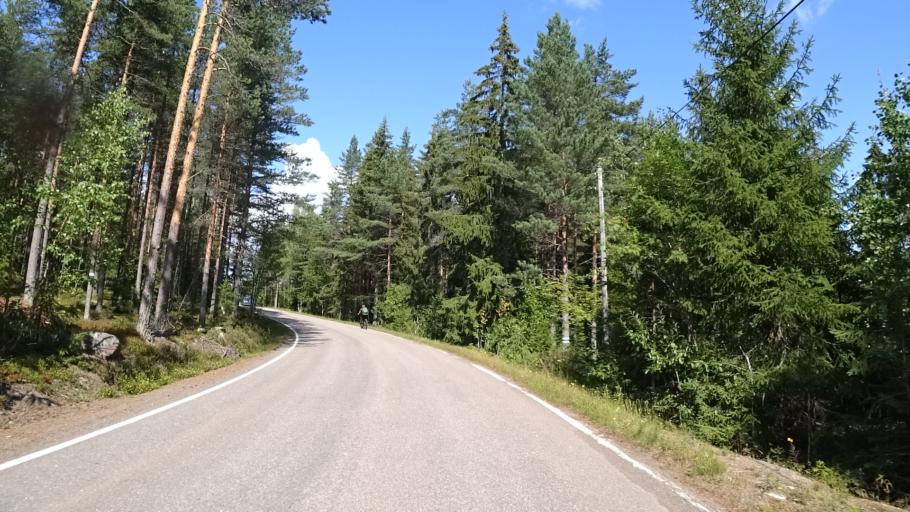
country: FI
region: Kymenlaakso
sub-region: Kotka-Hamina
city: Karhula
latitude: 60.5629
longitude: 26.9017
